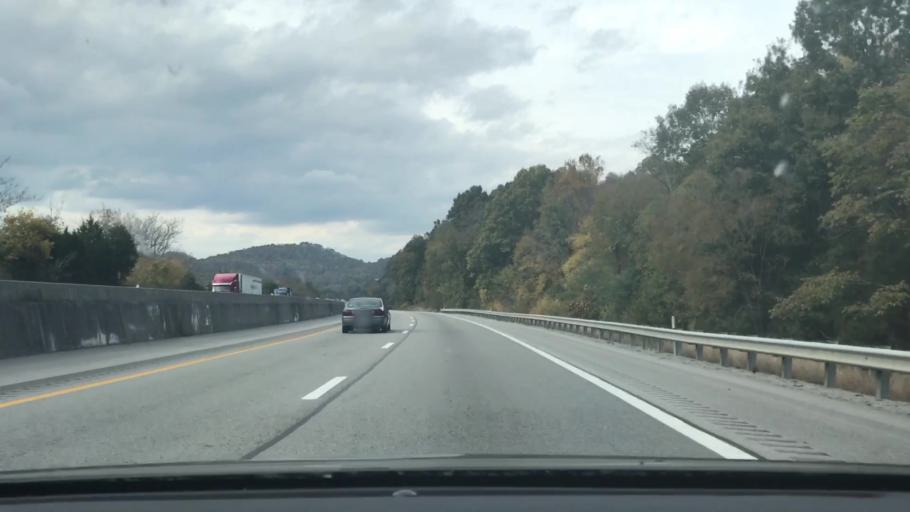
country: US
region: Tennessee
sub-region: Putnam County
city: Lafayette
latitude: 36.1305
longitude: -85.7796
